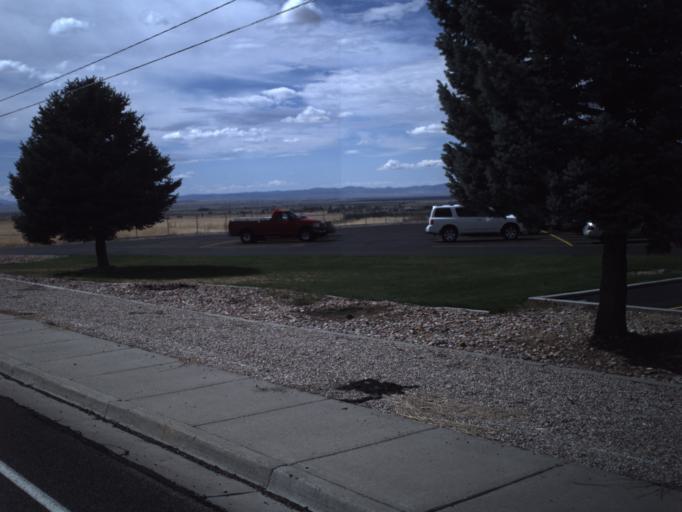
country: US
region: Utah
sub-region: Millard County
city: Fillmore
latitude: 38.9540
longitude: -112.3398
